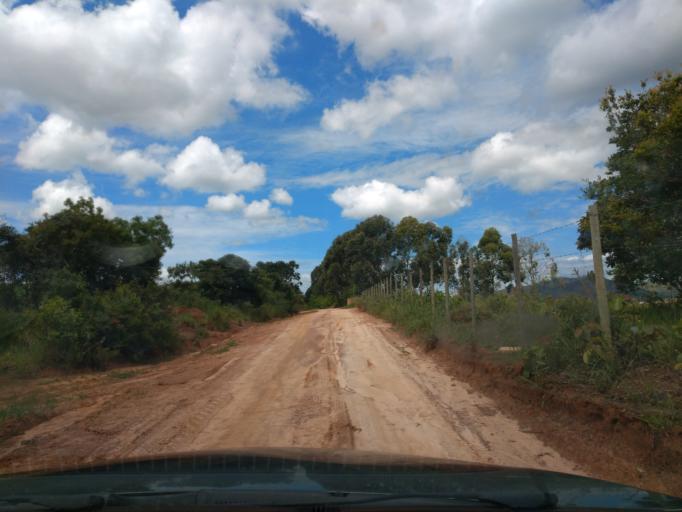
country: BR
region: Minas Gerais
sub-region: Lavras
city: Lavras
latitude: -21.5119
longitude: -44.9283
